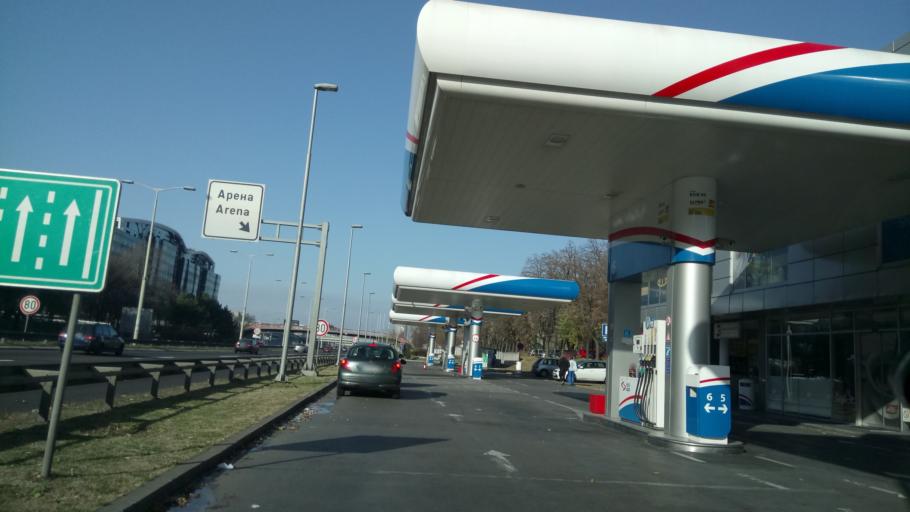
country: RS
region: Central Serbia
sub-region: Belgrade
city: Novi Beograd
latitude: 44.8094
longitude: 20.4272
